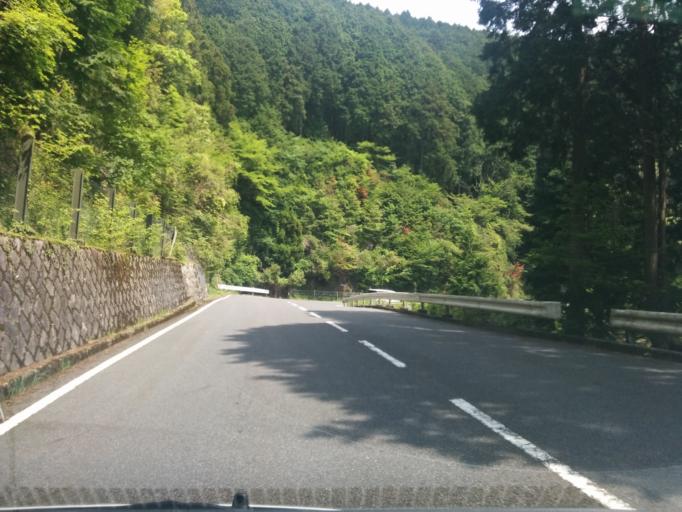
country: JP
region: Shiga Prefecture
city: Otsu-shi
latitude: 35.0622
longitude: 135.8365
